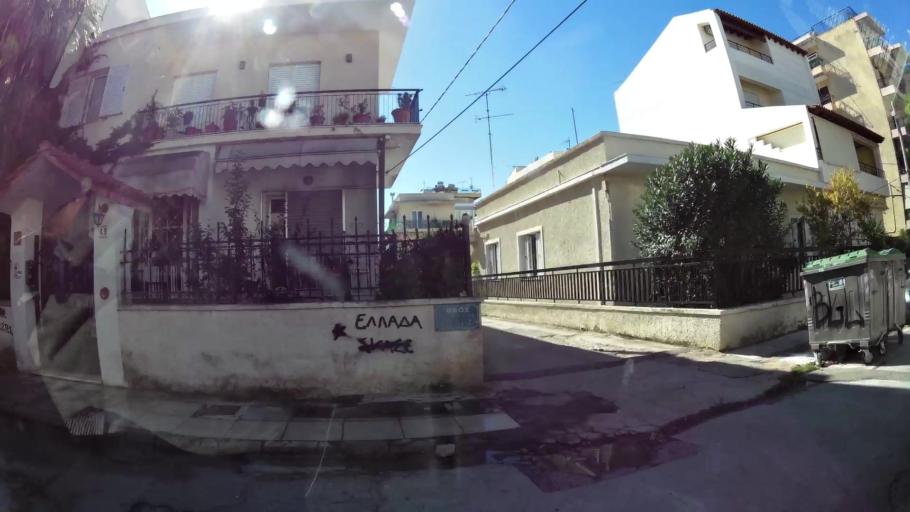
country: GR
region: Attica
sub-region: Nomarchia Athinas
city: Khalandrion
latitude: 38.0296
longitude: 23.8047
